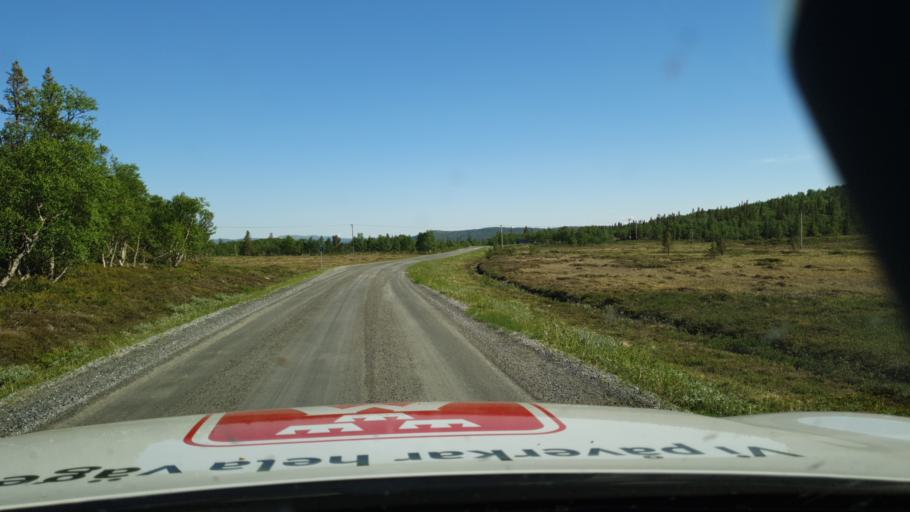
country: SE
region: Jaemtland
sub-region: Are Kommun
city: Are
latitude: 62.8857
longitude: 12.7226
